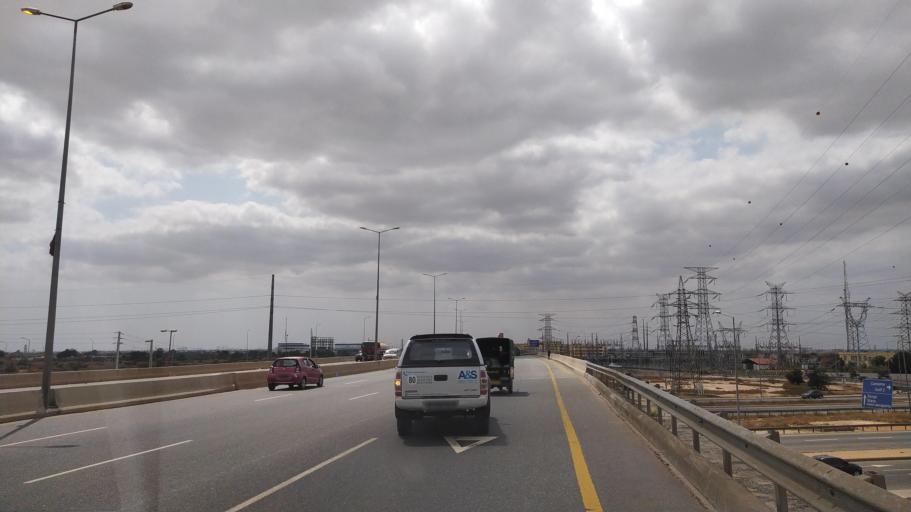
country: AO
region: Luanda
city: Luanda
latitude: -8.9742
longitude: 13.2539
